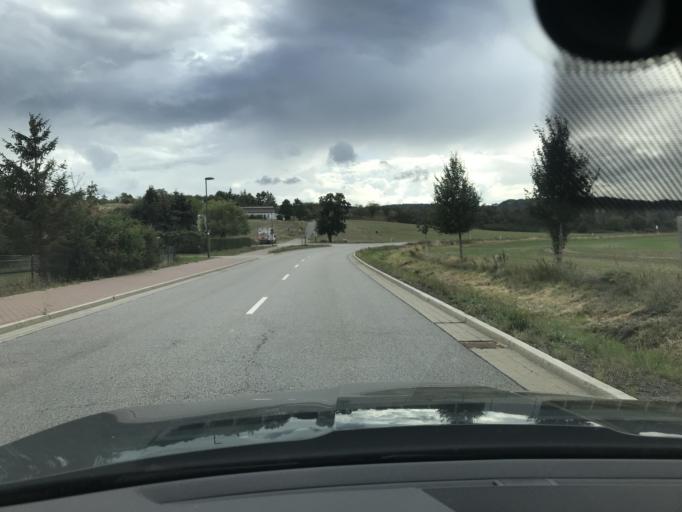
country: DE
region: Saxony-Anhalt
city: Thale
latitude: 51.7709
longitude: 11.0532
